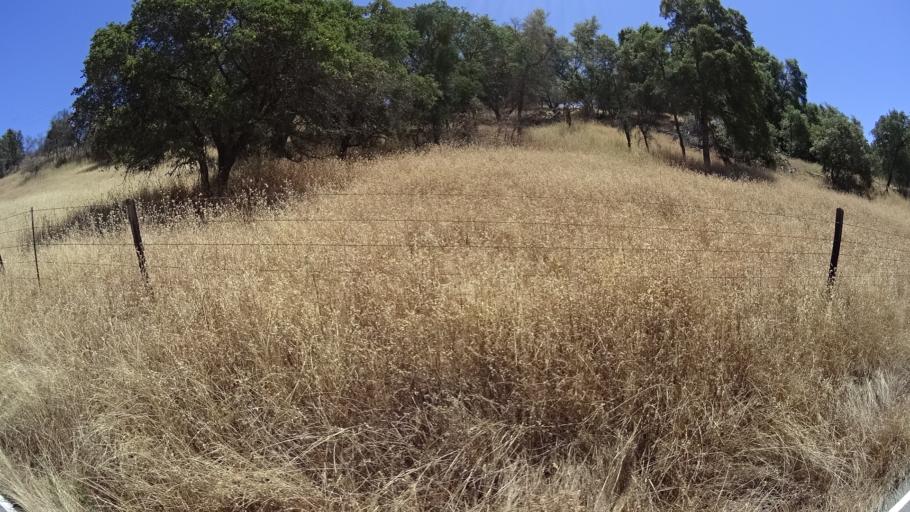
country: US
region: California
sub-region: Calaveras County
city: Valley Springs
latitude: 38.2459
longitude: -120.7819
